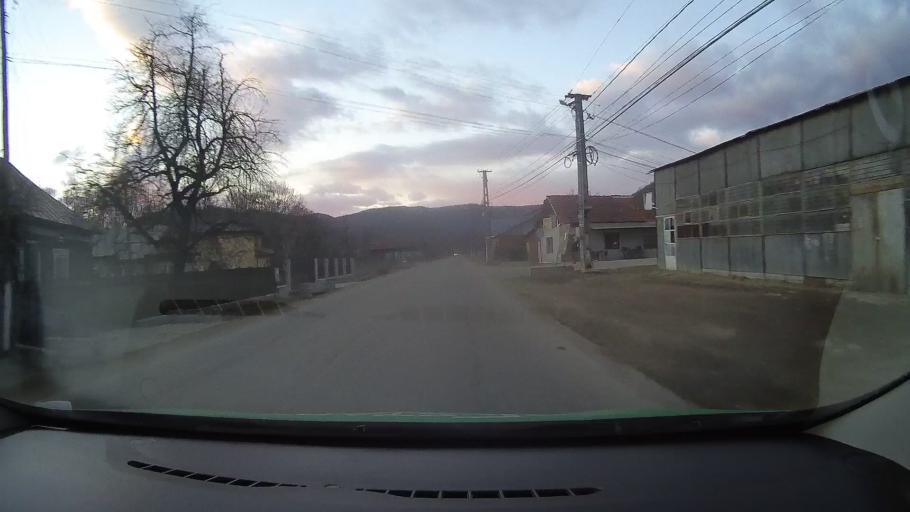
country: RO
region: Dambovita
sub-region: Comuna Valea Lunga
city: Valea Lunga-Cricov
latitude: 45.0671
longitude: 25.5834
